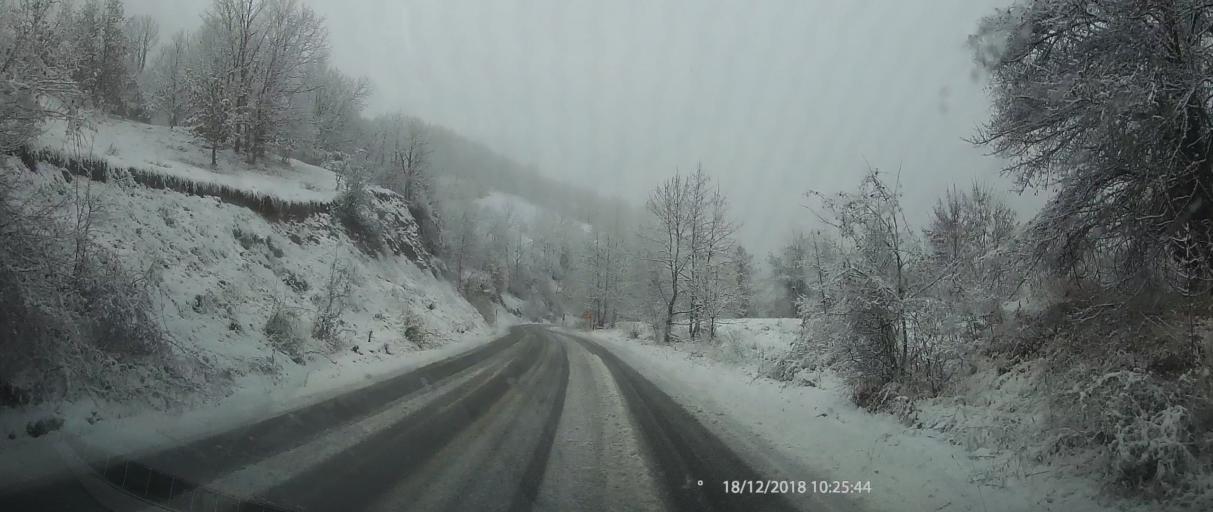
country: GR
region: Thessaly
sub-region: Nomos Larisis
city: Livadi
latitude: 40.1669
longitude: 22.2486
